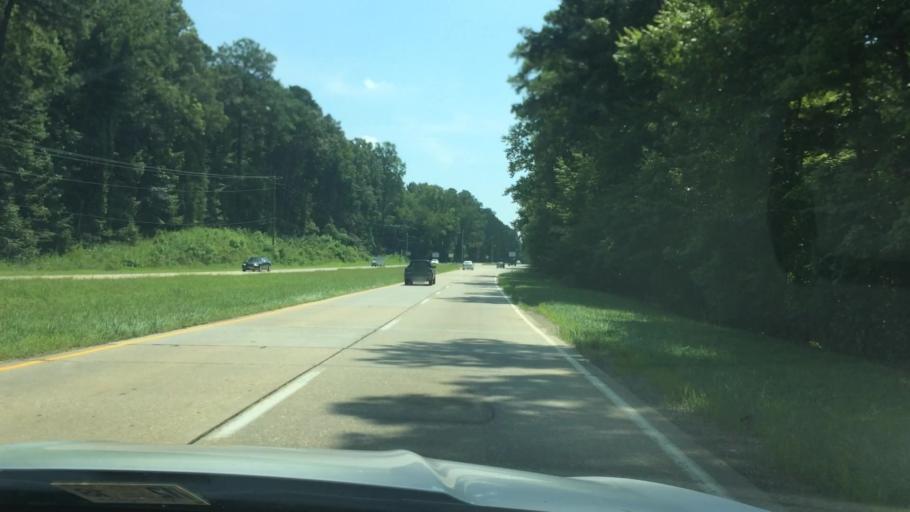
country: US
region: Virginia
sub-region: Charles City County
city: Charles City
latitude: 37.4822
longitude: -77.1323
